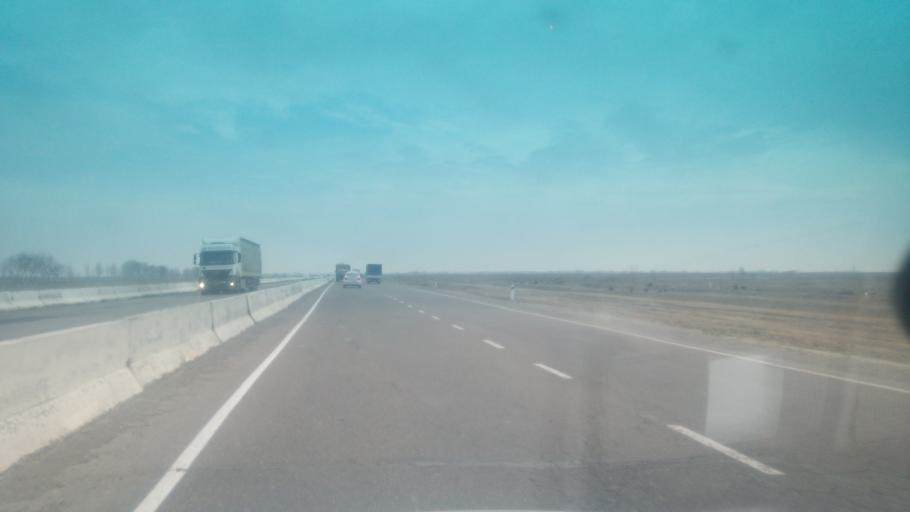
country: KZ
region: Ongtustik Qazaqstan
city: Myrzakent
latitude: 40.5140
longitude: 68.4866
